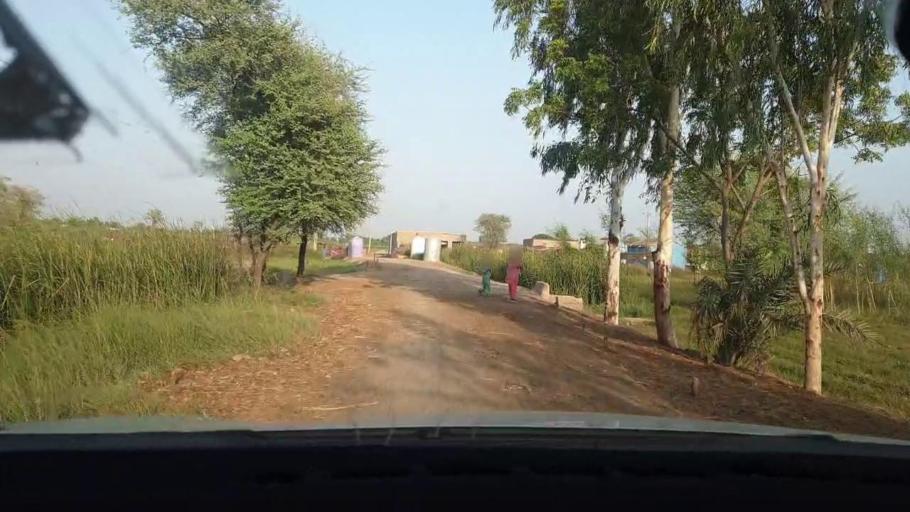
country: PK
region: Sindh
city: Shahdadpur
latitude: 25.8958
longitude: 68.6809
